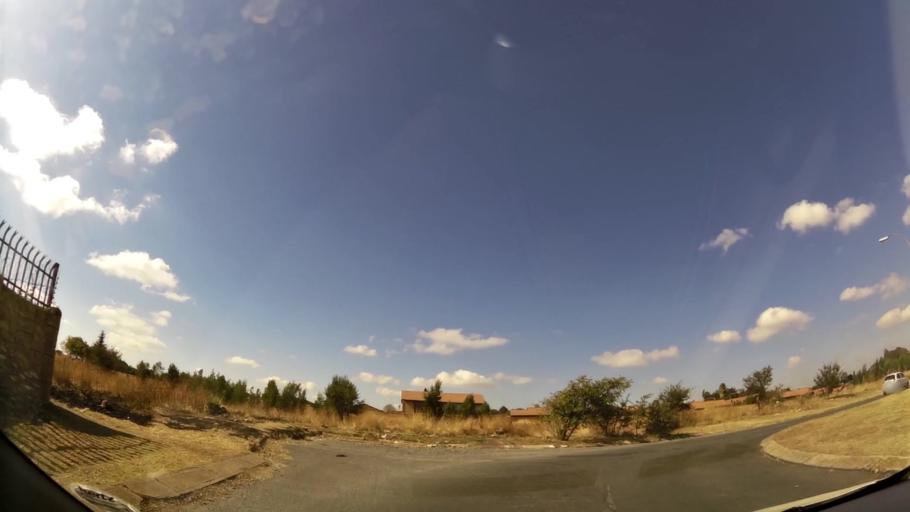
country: ZA
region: Gauteng
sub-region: City of Johannesburg Metropolitan Municipality
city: Roodepoort
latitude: -26.1221
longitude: 27.8417
